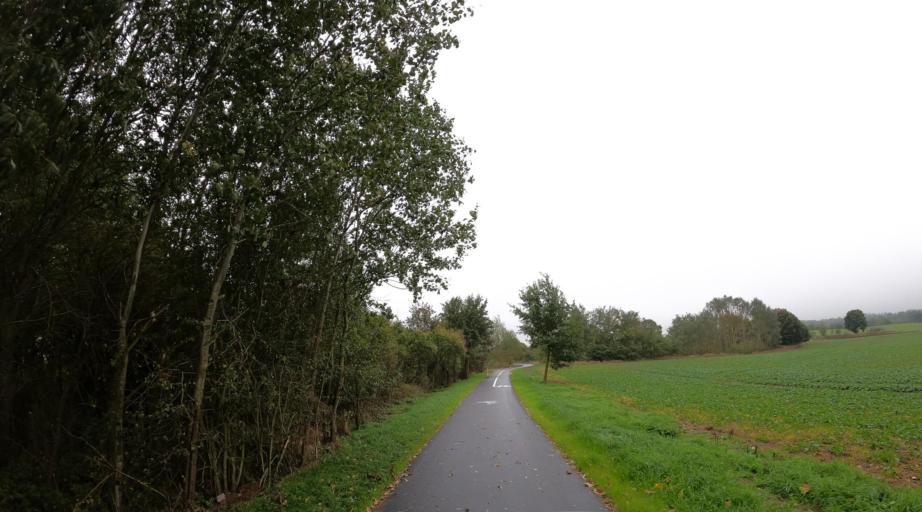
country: PL
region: West Pomeranian Voivodeship
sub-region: Powiat mysliborski
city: Mysliborz
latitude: 52.9208
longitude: 14.7396
